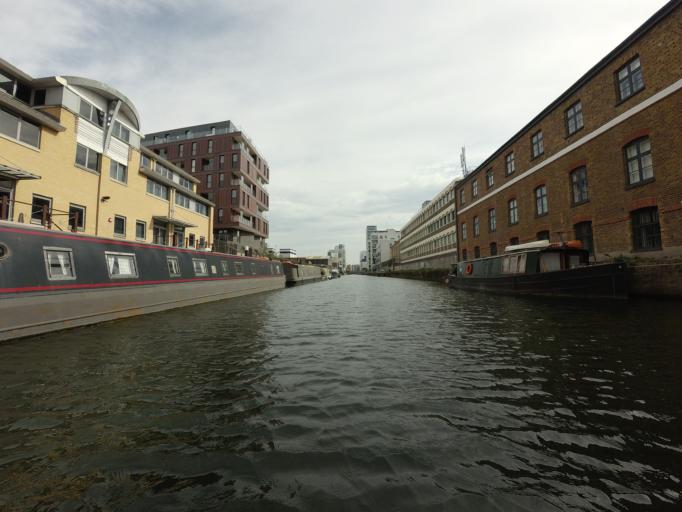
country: GB
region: England
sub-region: Greater London
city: Poplar
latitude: 51.5144
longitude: -0.0273
